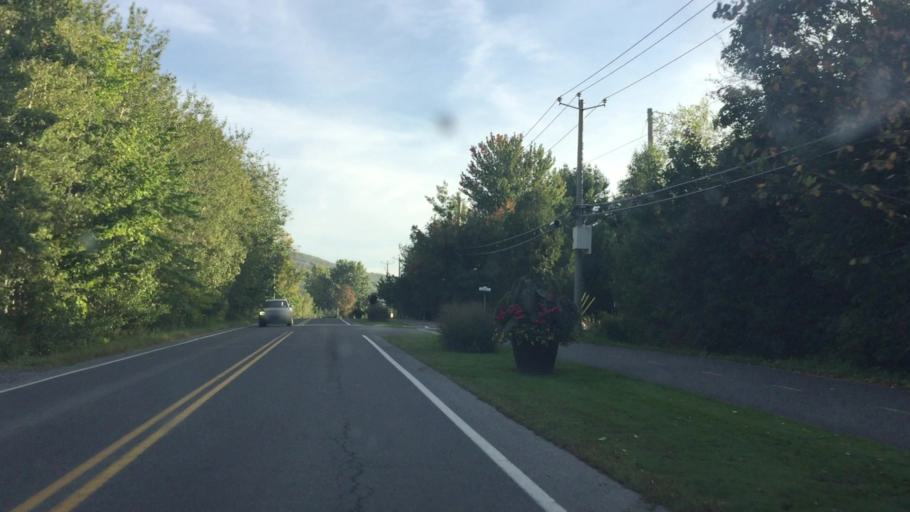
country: CA
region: Quebec
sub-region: Monteregie
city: Bromont
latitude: 45.3118
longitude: -72.6573
